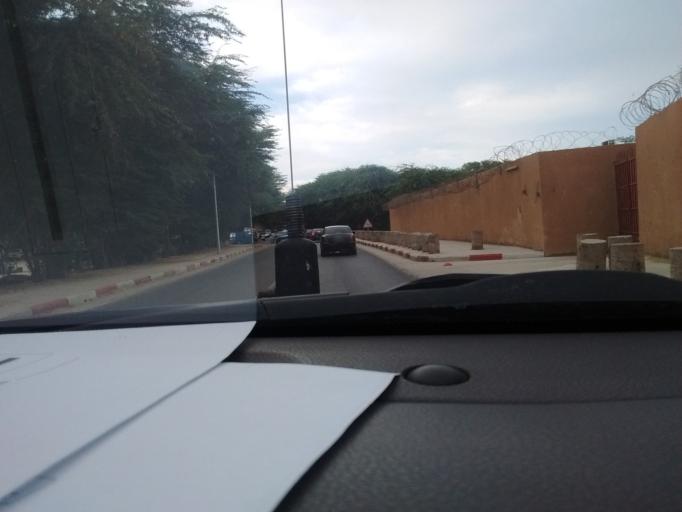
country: MR
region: Nouakchott
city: Nouakchott
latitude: 18.0930
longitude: -15.9833
